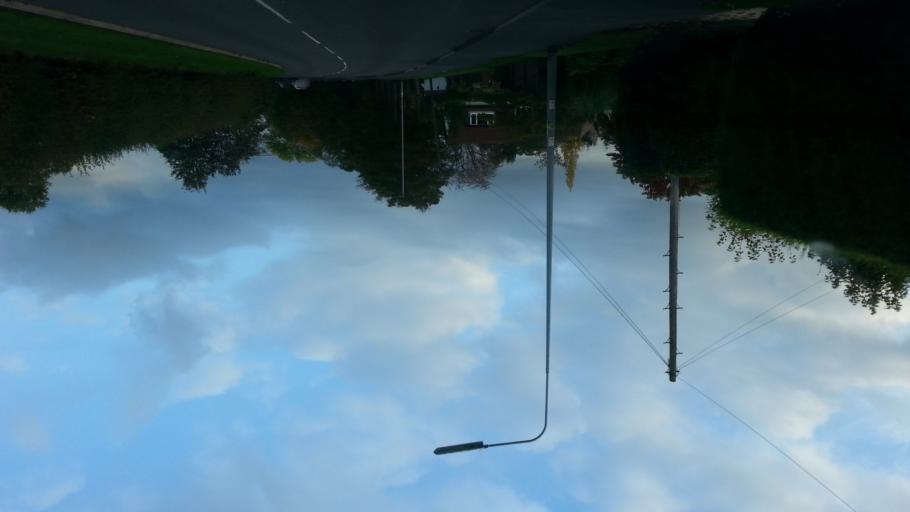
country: GB
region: England
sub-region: Staffordshire
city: Fazeley
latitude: 52.6169
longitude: -1.7354
